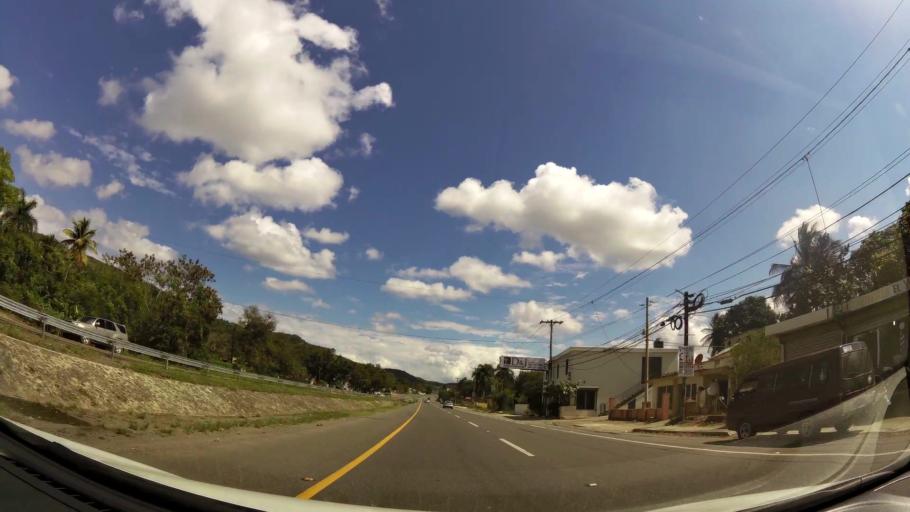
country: DO
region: La Vega
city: Rio Verde Arriba
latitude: 19.3010
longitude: -70.5834
